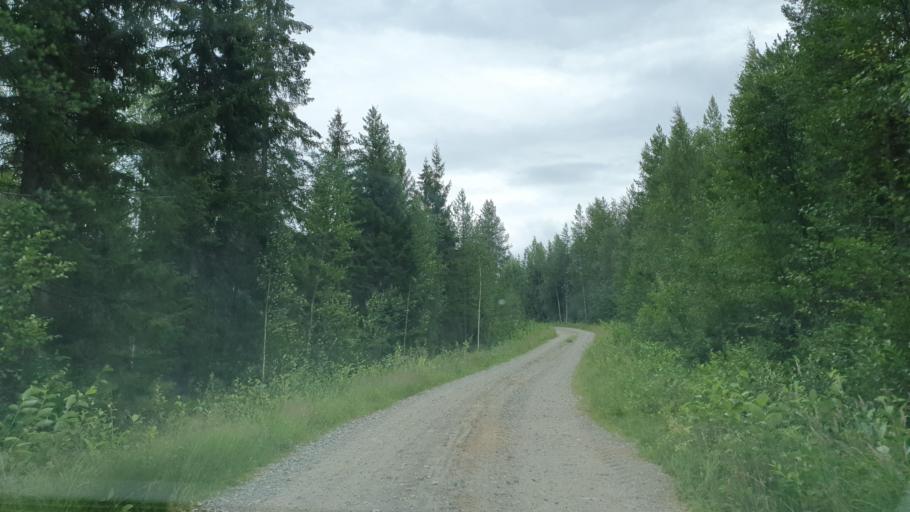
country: FI
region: Kainuu
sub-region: Kehys-Kainuu
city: Kuhmo
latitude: 64.2035
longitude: 29.4005
